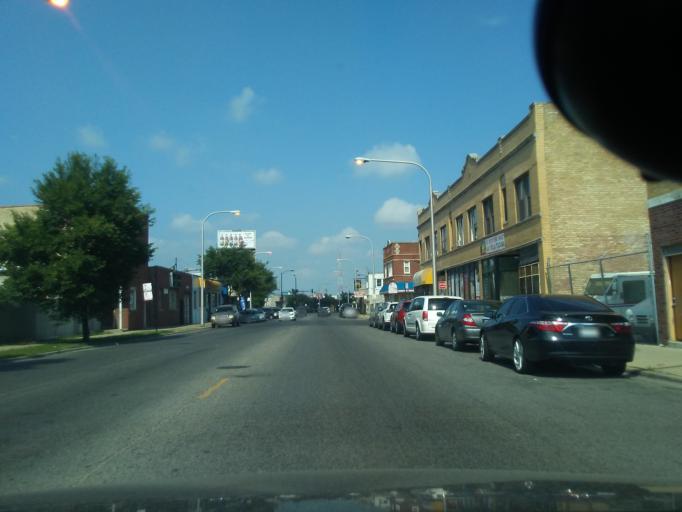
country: US
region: Illinois
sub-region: Cook County
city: Oak Park
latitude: 41.9169
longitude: -87.7538
